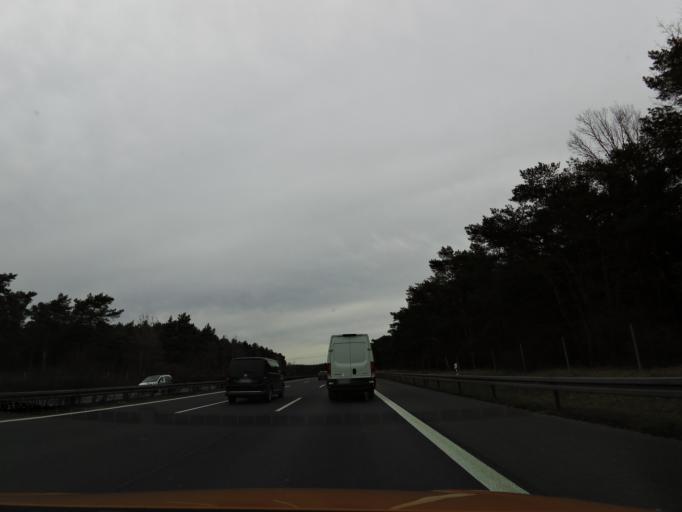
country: DE
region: Brandenburg
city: Beelitz
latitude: 52.2270
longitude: 12.9121
